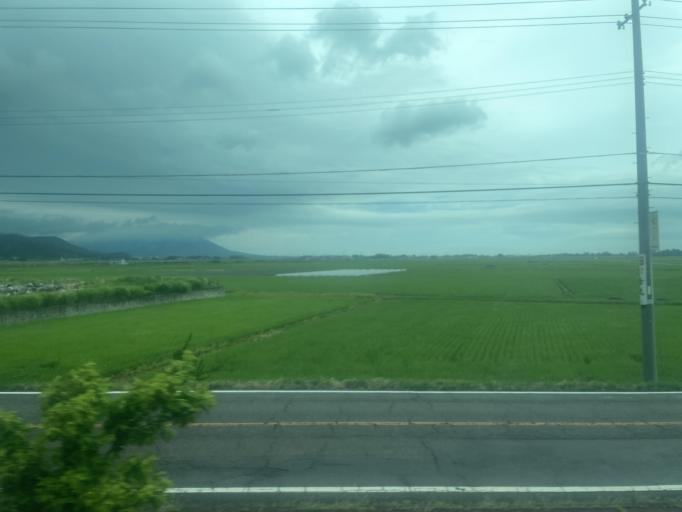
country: JP
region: Niigata
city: Yoshida-kasugacho
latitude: 37.6984
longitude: 138.8440
